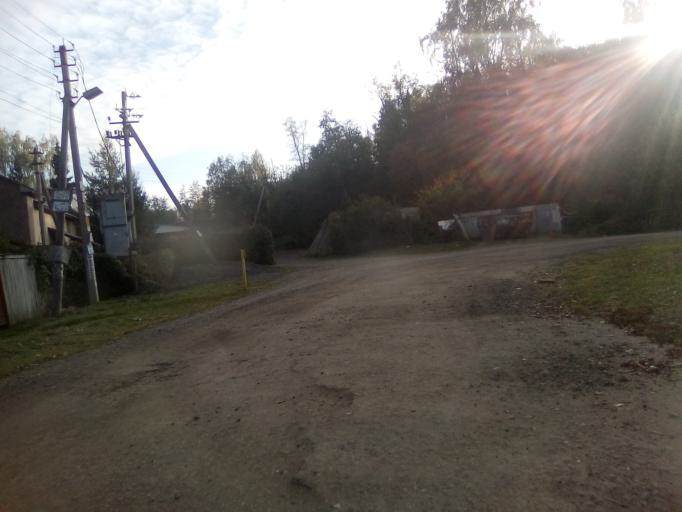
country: RU
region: Moskovskaya
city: Filimonki
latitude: 55.5440
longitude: 37.3845
